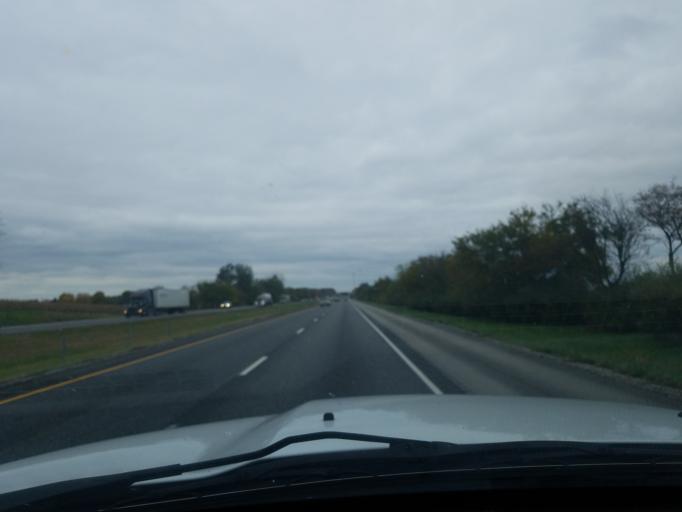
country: US
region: Indiana
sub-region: Johnson County
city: Franklin
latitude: 39.4372
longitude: -85.9829
